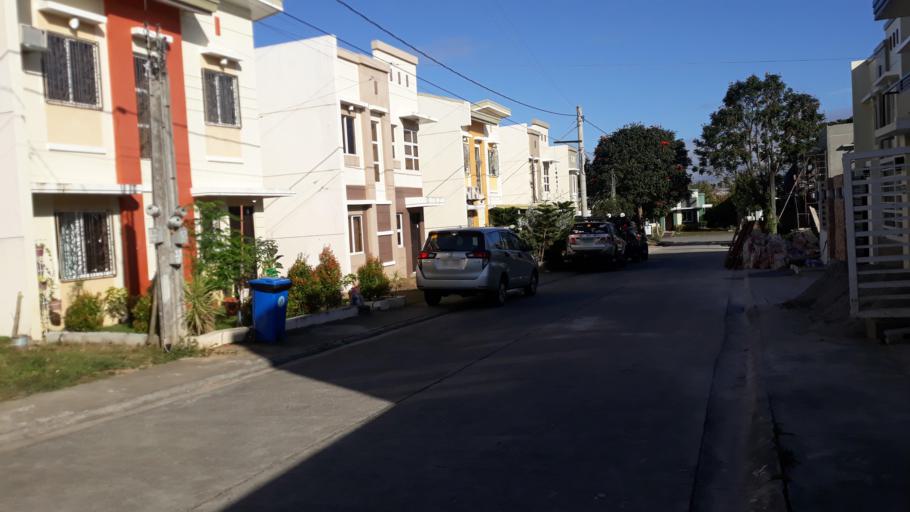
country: PH
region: Calabarzon
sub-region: Province of Cavite
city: Biga
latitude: 14.2743
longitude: 120.9667
